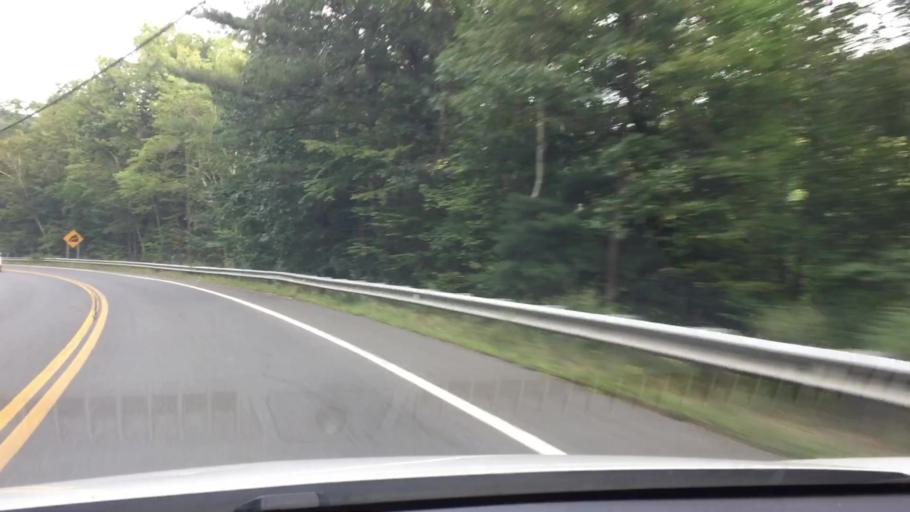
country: US
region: Massachusetts
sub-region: Hampden County
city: Granville
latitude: 42.1631
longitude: -72.8432
